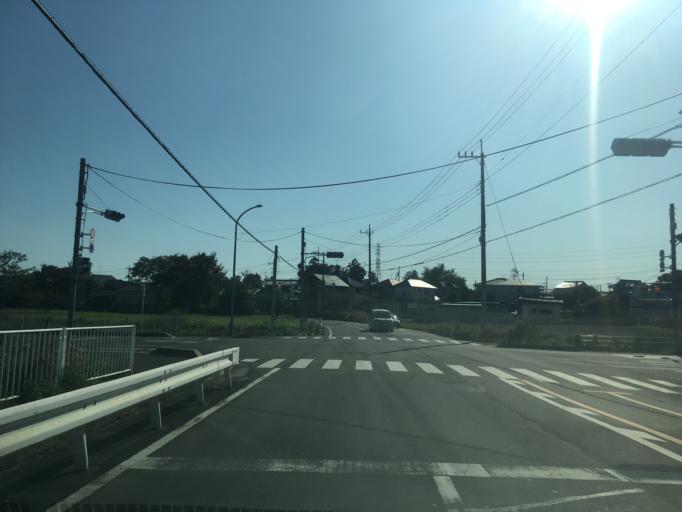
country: JP
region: Saitama
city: Sakado
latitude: 35.9618
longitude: 139.4454
